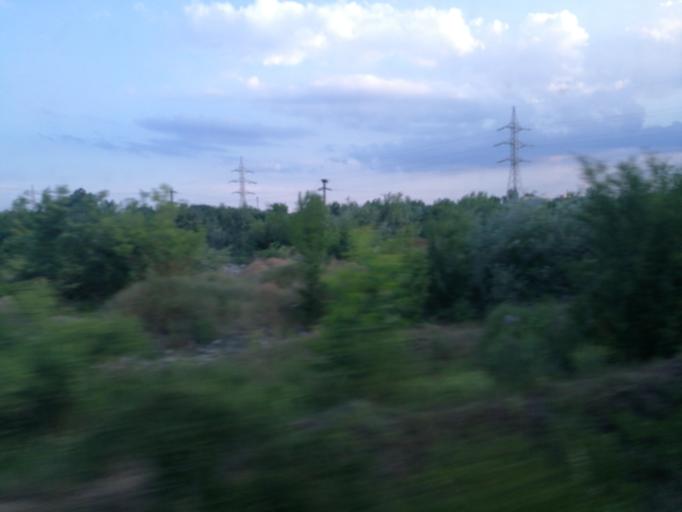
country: RO
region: Dambovita
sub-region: Comuna Titu
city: Salcuta
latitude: 44.6616
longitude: 25.5795
